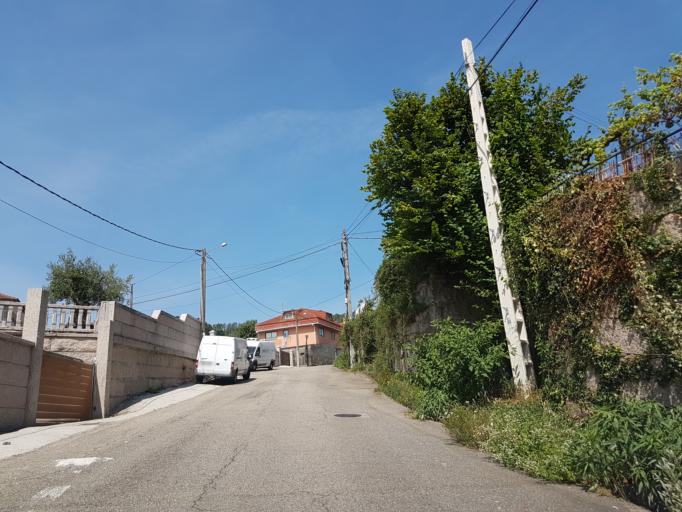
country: ES
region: Galicia
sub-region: Provincia de Pontevedra
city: Porrino
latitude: 42.2203
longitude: -8.6208
